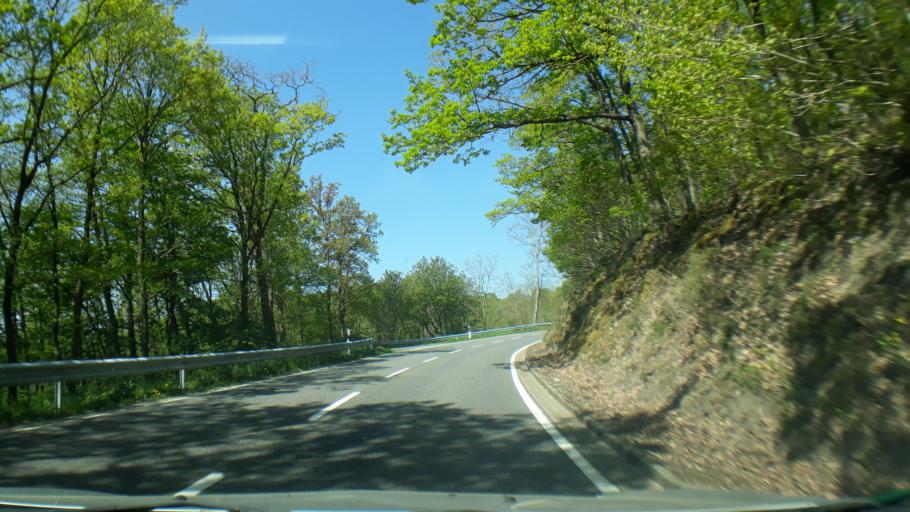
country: DE
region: North Rhine-Westphalia
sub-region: Regierungsbezirk Koln
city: Nideggen
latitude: 50.6821
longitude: 6.4312
